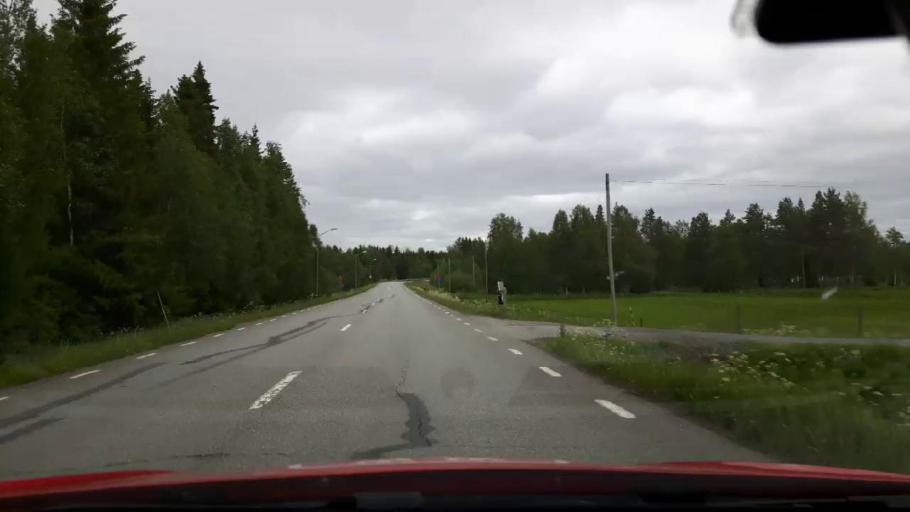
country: SE
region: Jaemtland
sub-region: Stroemsunds Kommun
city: Stroemsund
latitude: 63.5381
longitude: 15.4400
